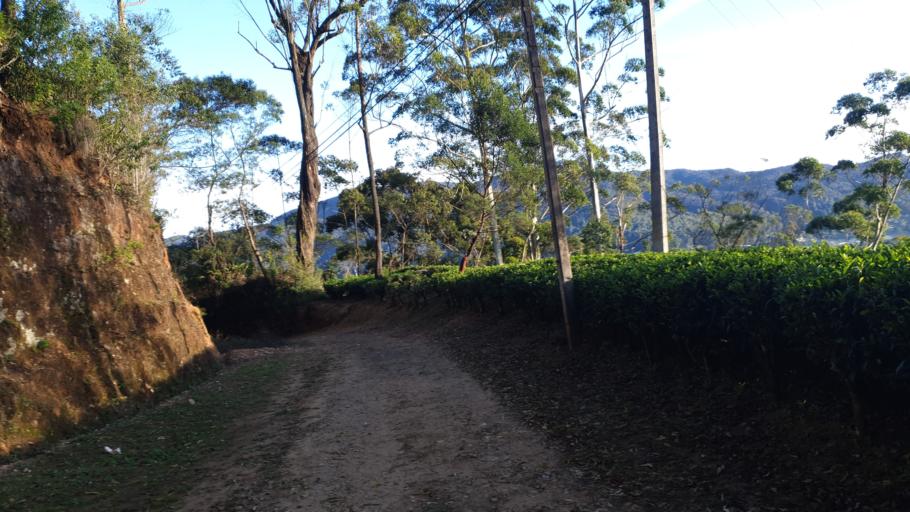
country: LK
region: Central
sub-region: Nuwara Eliya District
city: Nuwara Eliya
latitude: 6.9579
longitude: 80.7631
